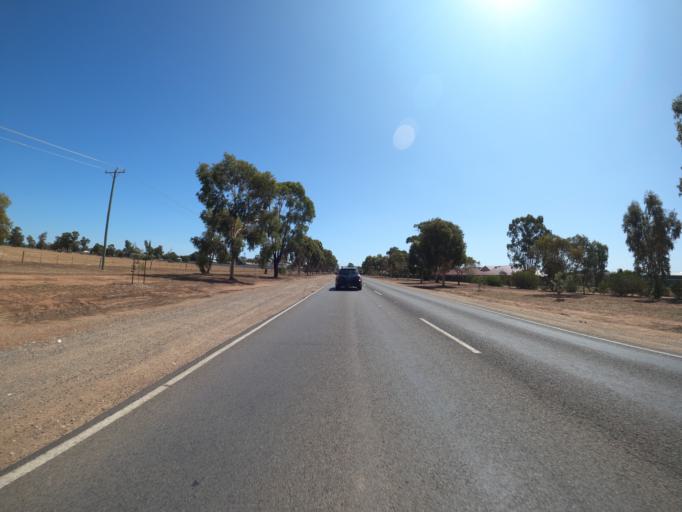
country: AU
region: Victoria
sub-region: Moira
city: Yarrawonga
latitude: -36.0141
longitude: 146.0164
